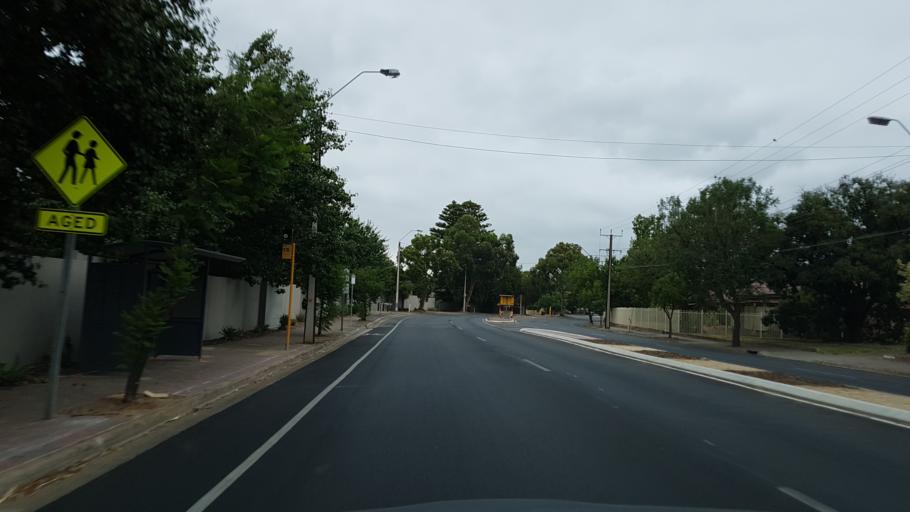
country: AU
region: South Australia
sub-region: Norwood Payneham St Peters
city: Marden
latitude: -34.8919
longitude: 138.6404
